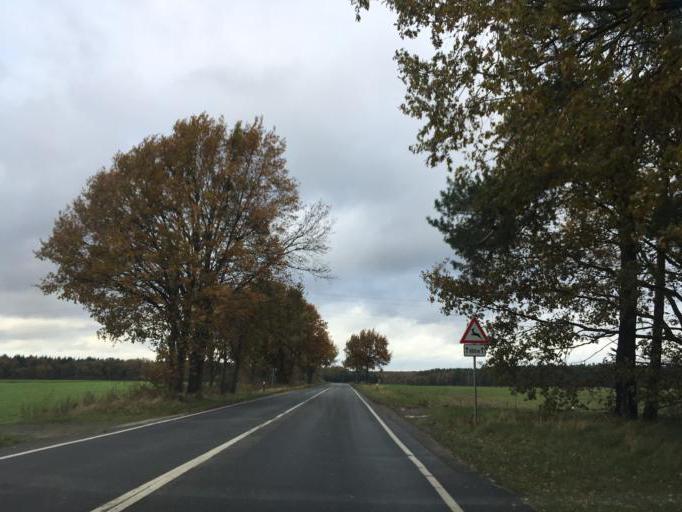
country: DE
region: Lower Saxony
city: Deutsch Evern
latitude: 53.2062
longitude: 10.4482
